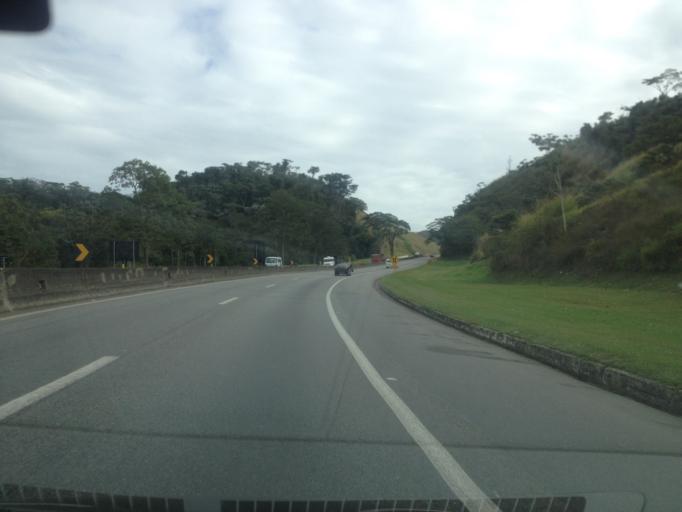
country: BR
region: Rio de Janeiro
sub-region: Pirai
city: Pirai
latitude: -22.6239
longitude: -43.9206
